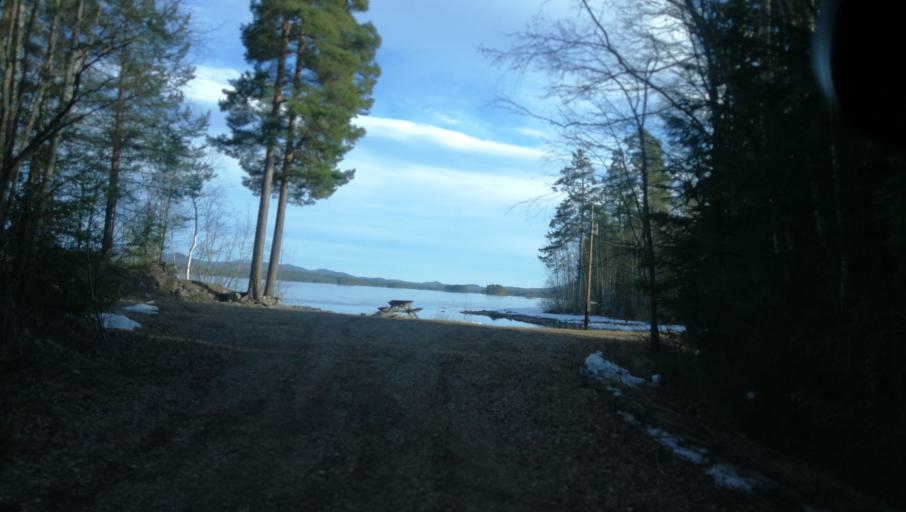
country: SE
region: Dalarna
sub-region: Vansbro Kommun
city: Vansbro
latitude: 60.7952
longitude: 14.2346
